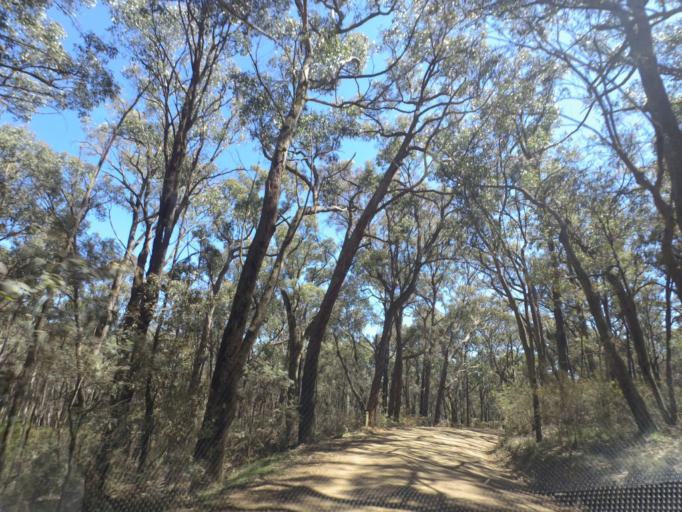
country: AU
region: Victoria
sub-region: Hume
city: Sunbury
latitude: -37.3877
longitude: 144.5609
